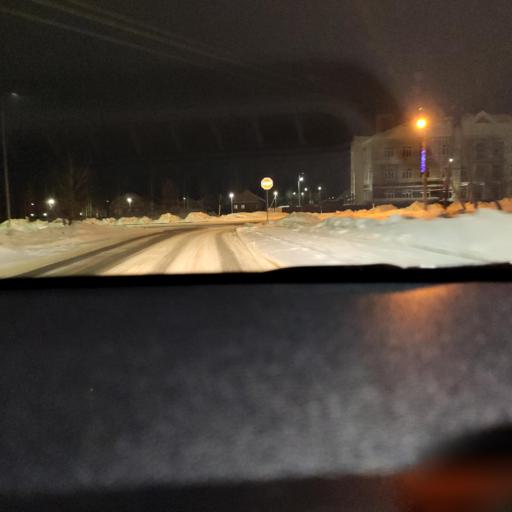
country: RU
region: Tatarstan
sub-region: Chistopol'skiy Rayon
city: Chistopol'
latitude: 55.3615
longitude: 50.5823
